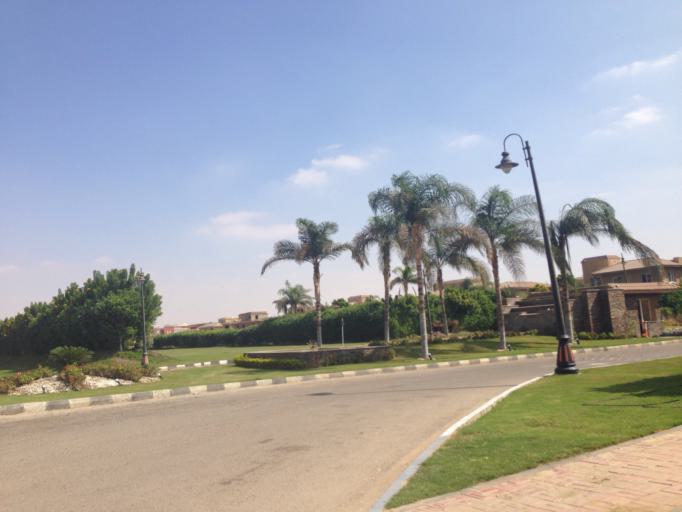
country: EG
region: Muhafazat al Qalyubiyah
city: Al Khankah
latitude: 30.0614
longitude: 31.4186
